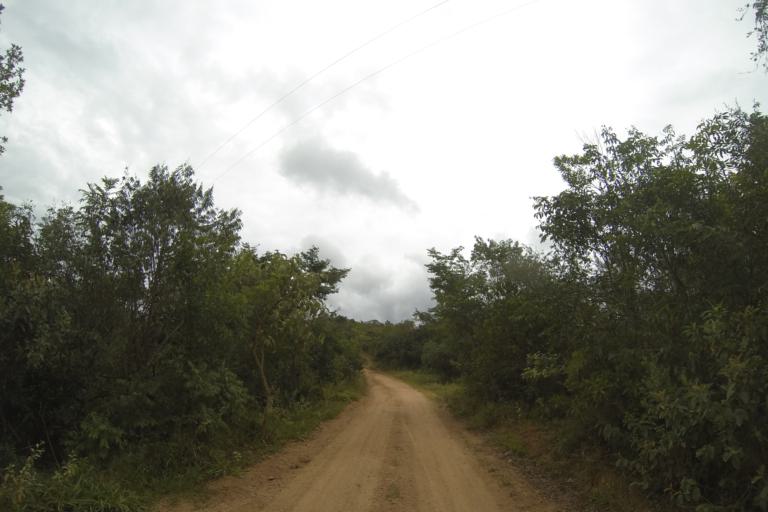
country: BR
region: Minas Gerais
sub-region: Ibia
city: Ibia
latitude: -19.7421
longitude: -46.5508
